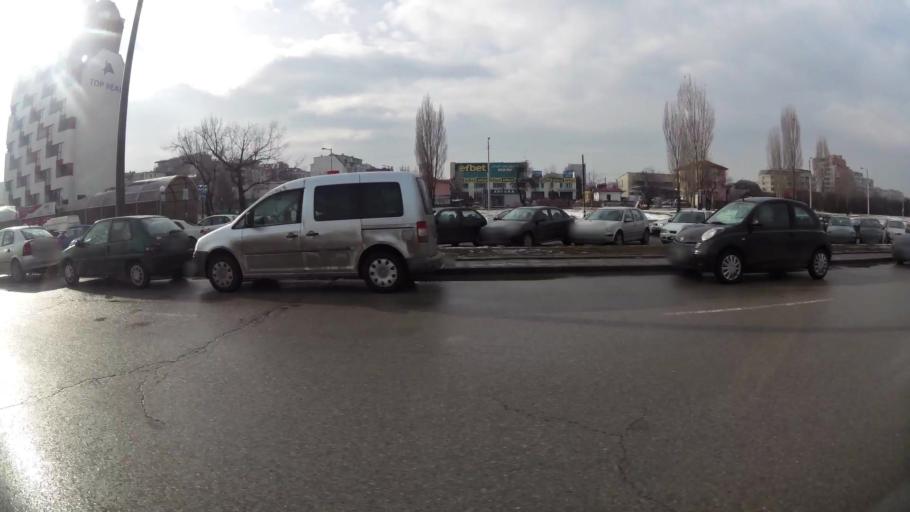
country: BG
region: Sofiya
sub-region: Obshtina Bozhurishte
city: Bozhurishte
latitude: 42.7186
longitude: 23.2568
